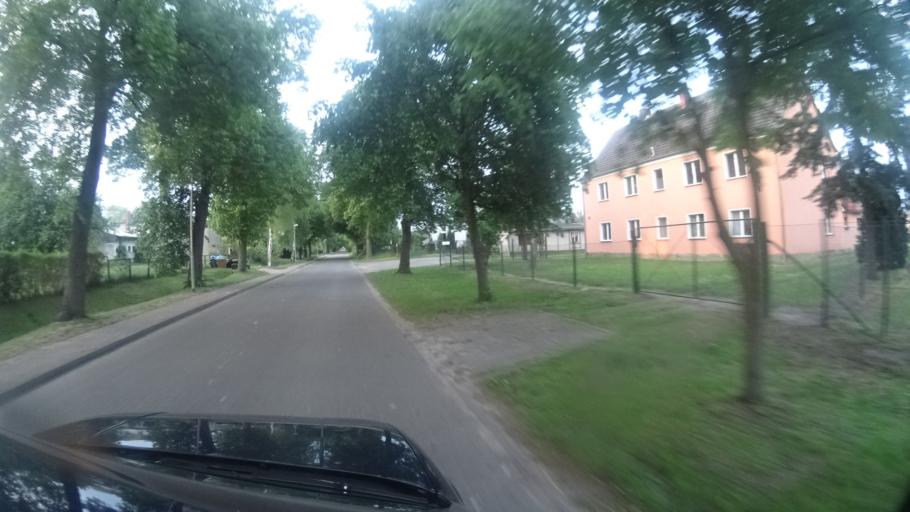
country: DE
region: Brandenburg
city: Ruthnick
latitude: 52.8216
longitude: 12.9618
